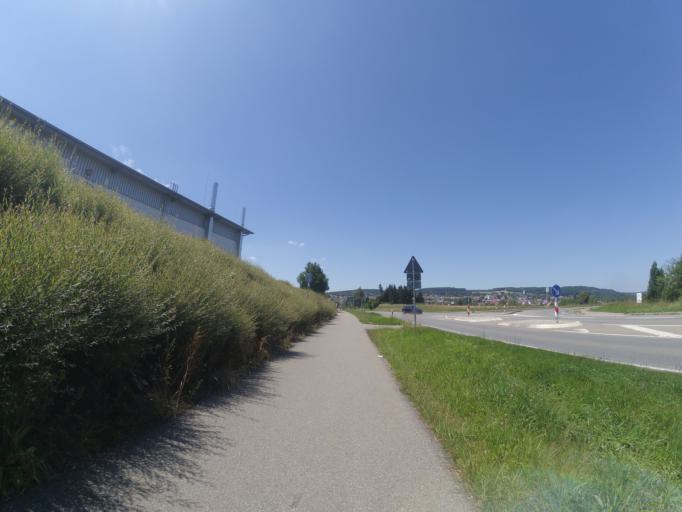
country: DE
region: Baden-Wuerttemberg
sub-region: Tuebingen Region
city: Aulendorf
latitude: 47.9418
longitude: 9.6494
